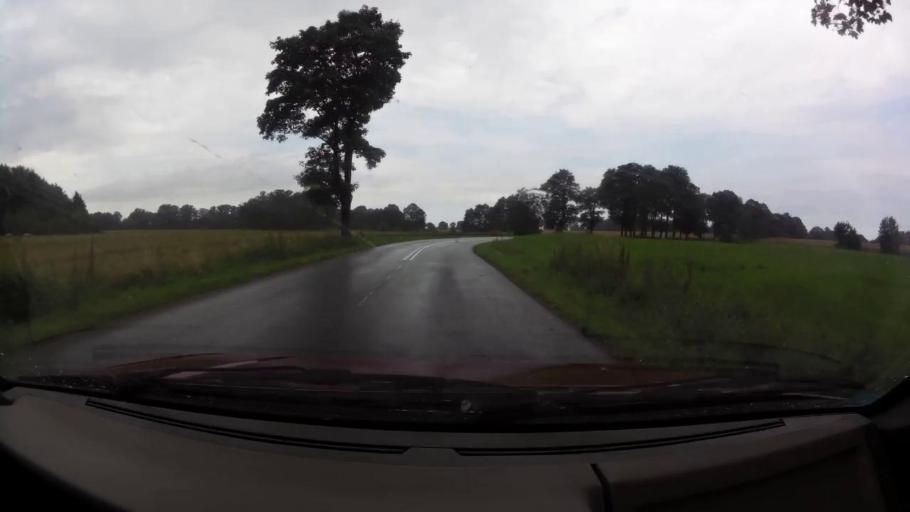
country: PL
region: West Pomeranian Voivodeship
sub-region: Koszalin
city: Koszalin
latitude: 54.1285
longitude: 16.1194
